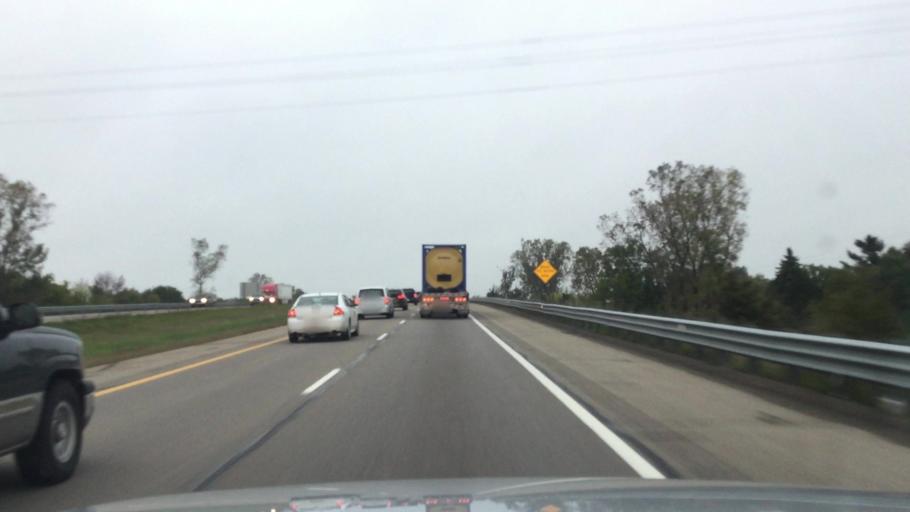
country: US
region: Michigan
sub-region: Shiawassee County
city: Durand
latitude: 42.9255
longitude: -84.0077
